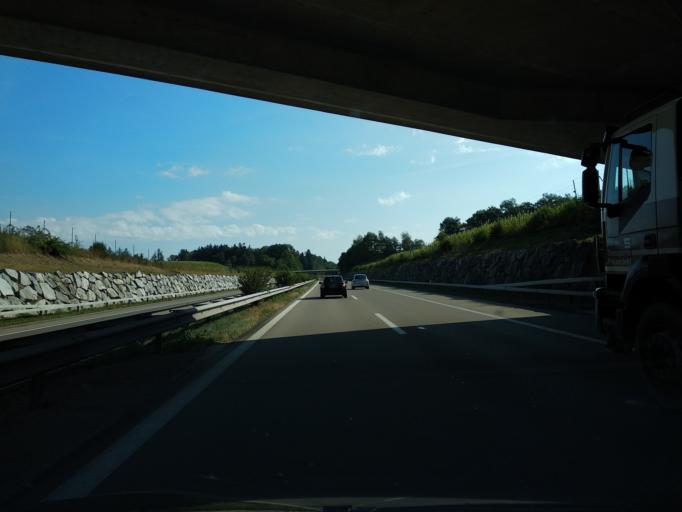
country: CH
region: Thurgau
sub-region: Kreuzlingen District
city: Tagerwilen
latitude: 47.6182
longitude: 9.1106
